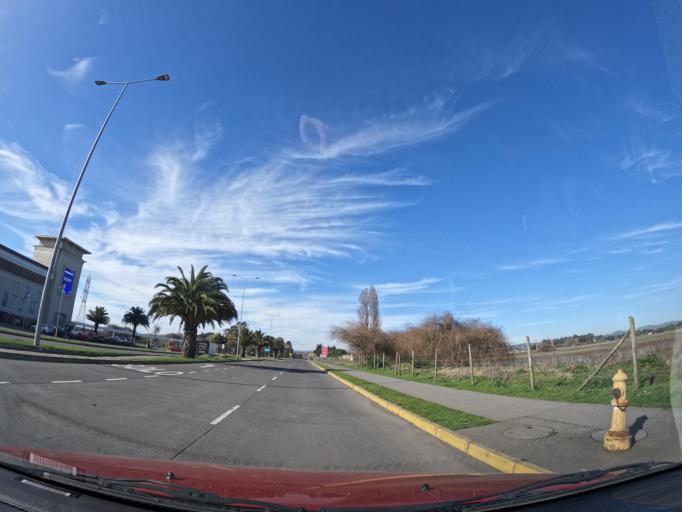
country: CL
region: Biobio
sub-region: Provincia de Concepcion
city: Concepcion
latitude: -36.7775
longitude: -73.0728
